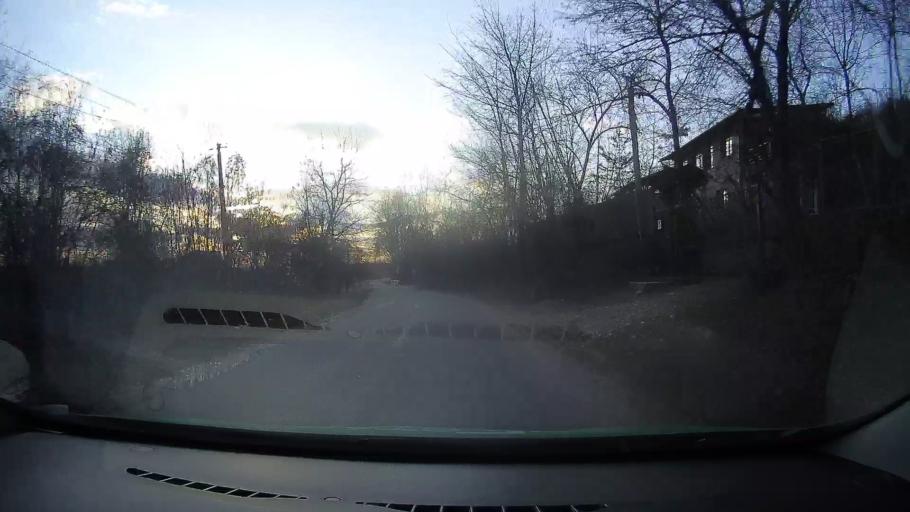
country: RO
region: Dambovita
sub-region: Comuna Gura Ocnitei
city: Adanca
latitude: 44.9360
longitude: 25.5912
